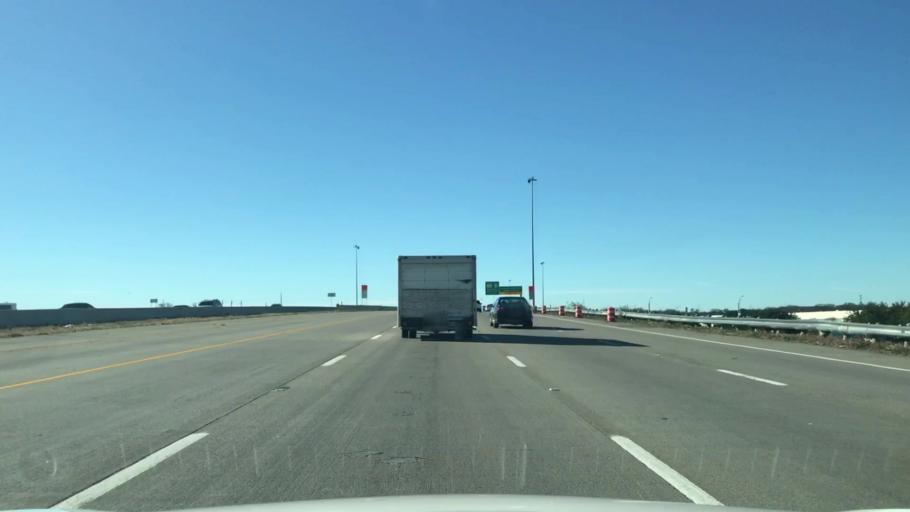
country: US
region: Texas
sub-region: Dallas County
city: Coppell
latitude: 32.9819
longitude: -97.0193
